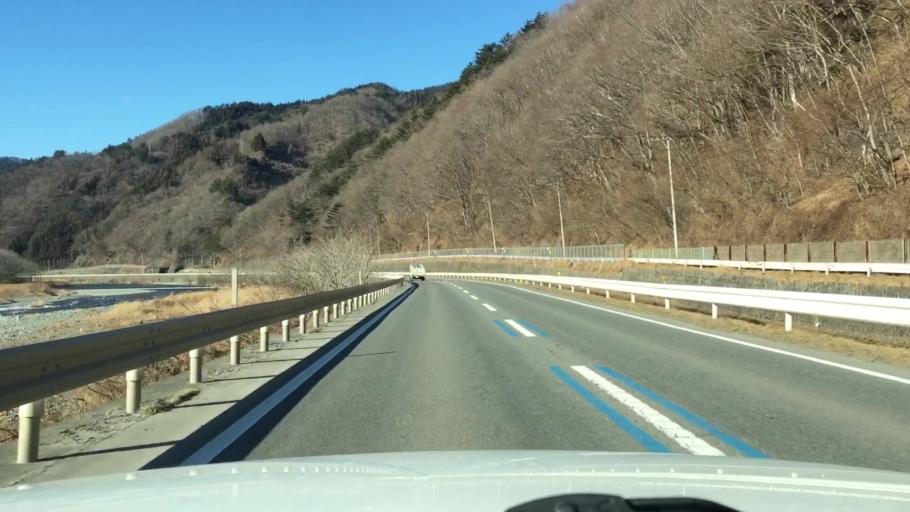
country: JP
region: Iwate
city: Miyako
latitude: 39.6315
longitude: 141.8535
